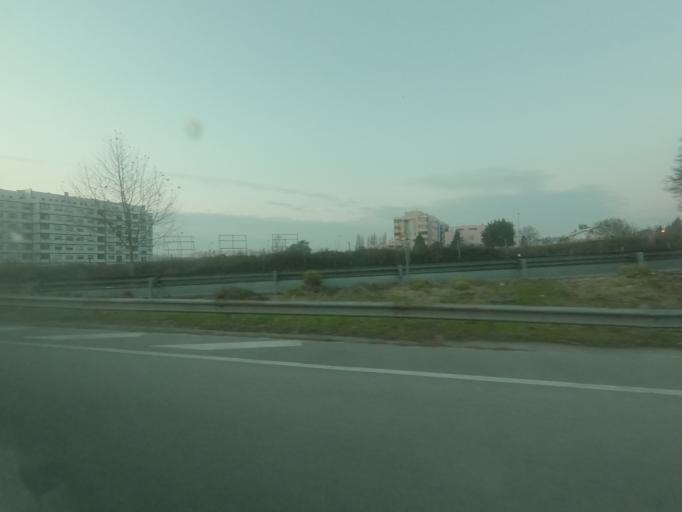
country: PT
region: Porto
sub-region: Matosinhos
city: Sao Mamede de Infesta
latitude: 41.1803
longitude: -8.6231
